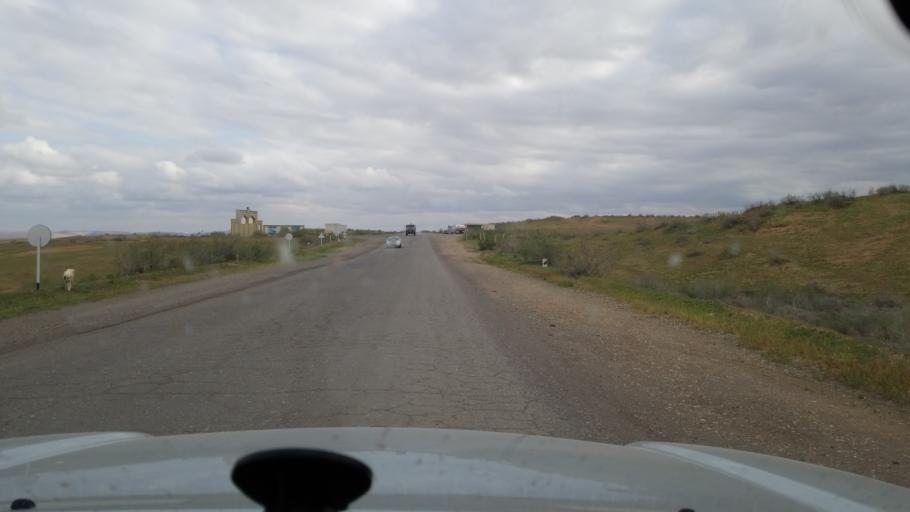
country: TM
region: Mary
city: Serhetabat
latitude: 35.9876
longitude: 62.6269
